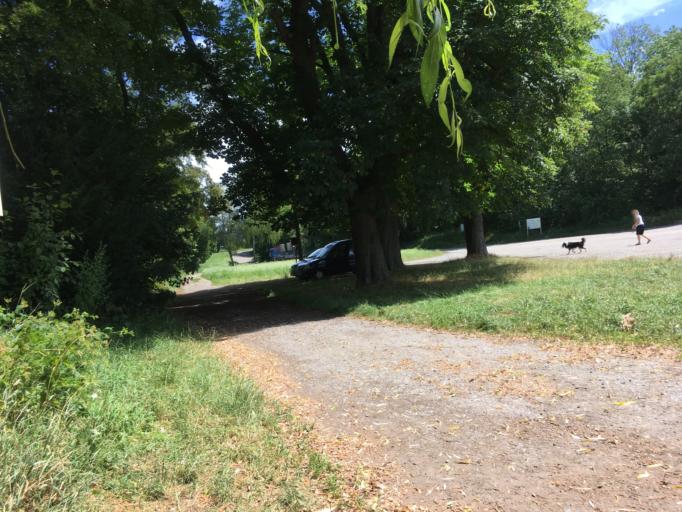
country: DE
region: Baden-Wuerttemberg
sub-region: Regierungsbezirk Stuttgart
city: Vaihingen an der Enz
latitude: 48.9193
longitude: 8.9757
